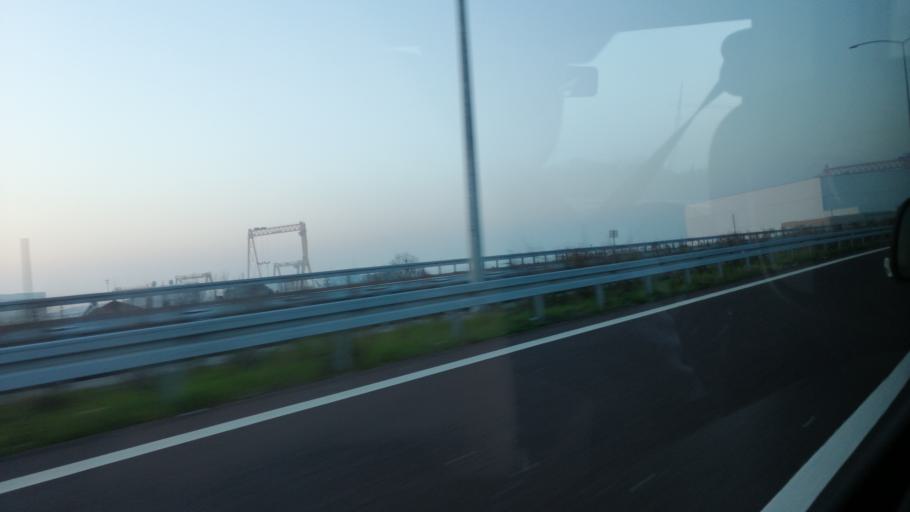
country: TR
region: Yalova
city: Altinova
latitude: 40.7239
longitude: 29.5032
